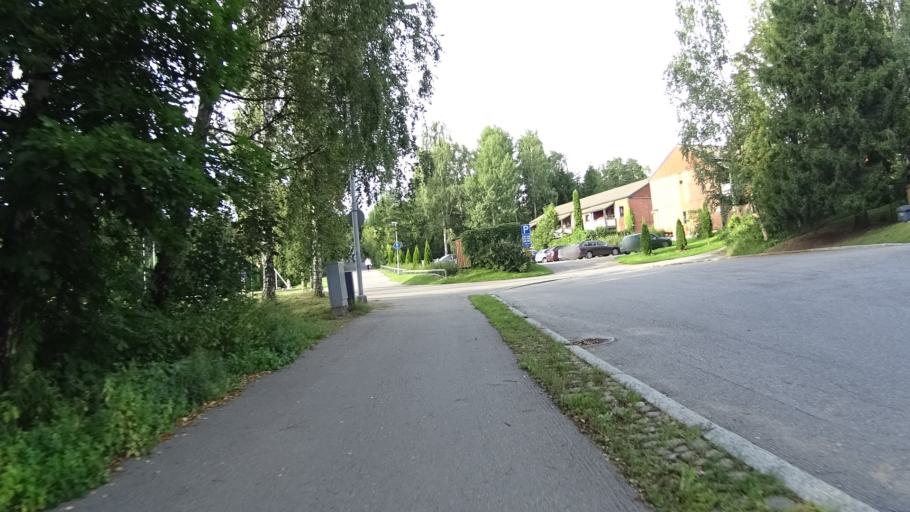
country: FI
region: Uusimaa
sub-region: Helsinki
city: Teekkarikylae
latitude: 60.2330
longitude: 24.8776
